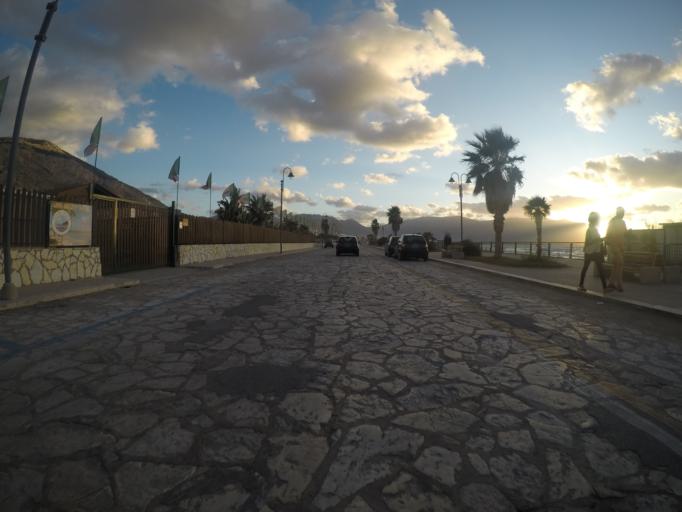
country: IT
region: Sicily
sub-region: Palermo
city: Isola delle Femmine
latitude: 38.1906
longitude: 13.2430
